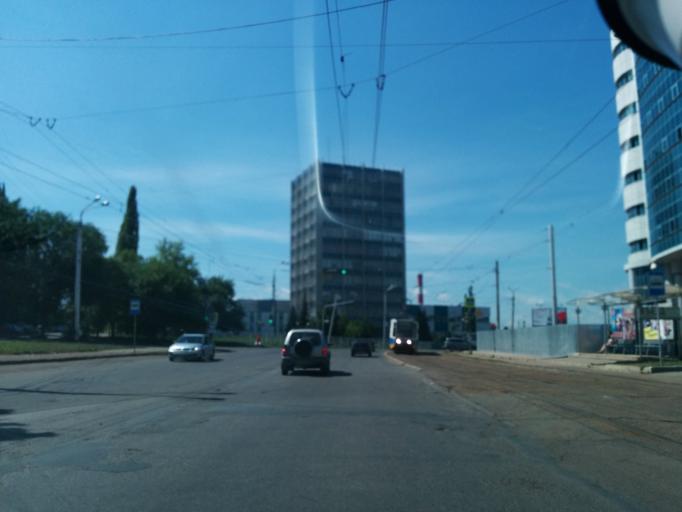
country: RU
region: Bashkortostan
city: Ufa
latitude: 54.7476
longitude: 55.9826
